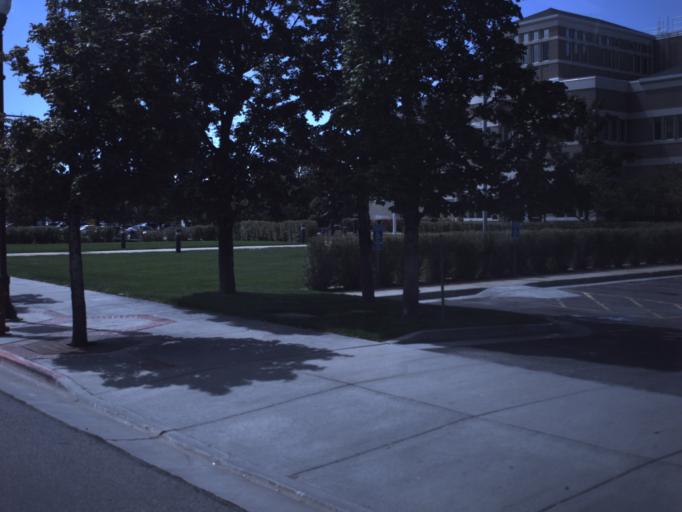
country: US
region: Utah
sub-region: Box Elder County
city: Brigham City
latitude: 41.5118
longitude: -112.0158
